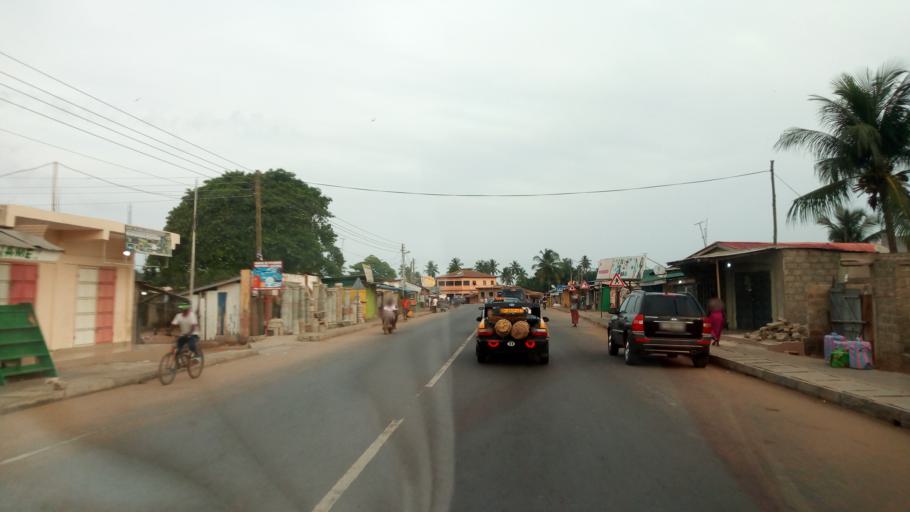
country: TG
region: Maritime
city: Lome
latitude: 6.1211
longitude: 1.1862
